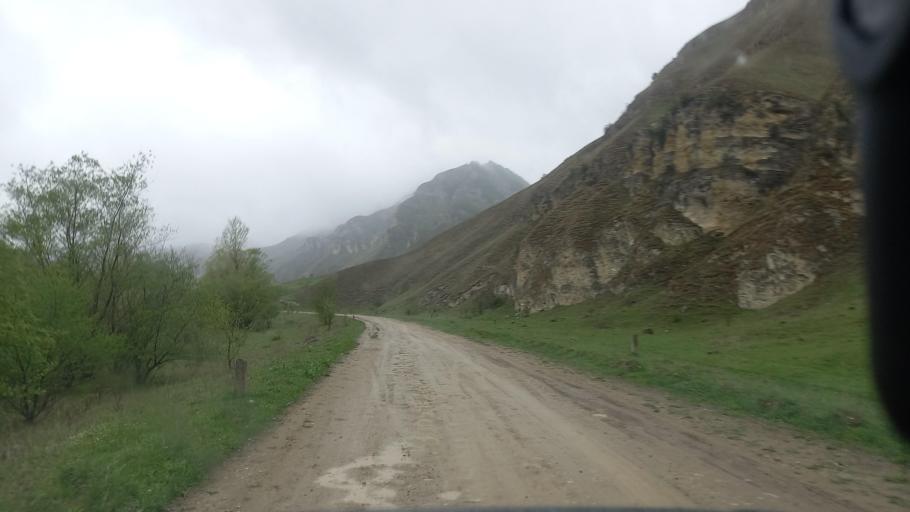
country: RU
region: Kabardino-Balkariya
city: Gundelen
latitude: 43.5983
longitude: 43.0596
